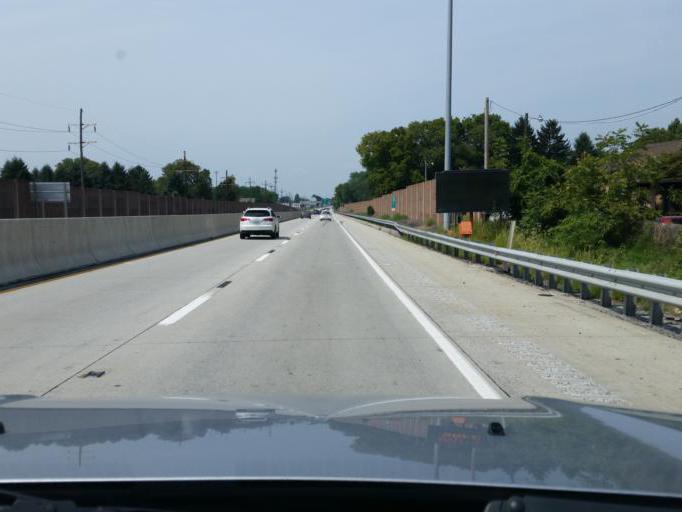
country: US
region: Pennsylvania
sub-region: Cumberland County
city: Shiremanstown
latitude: 40.2334
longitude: -76.9583
